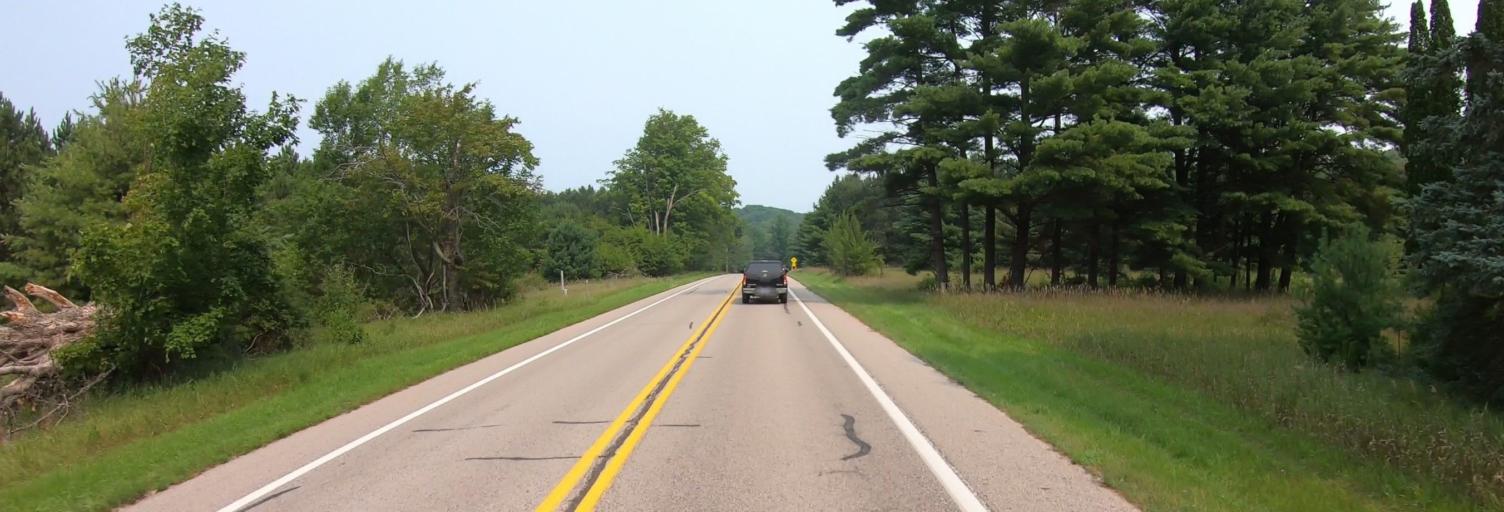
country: US
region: Michigan
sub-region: Leelanau County
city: Leland
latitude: 44.9294
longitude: -85.9472
